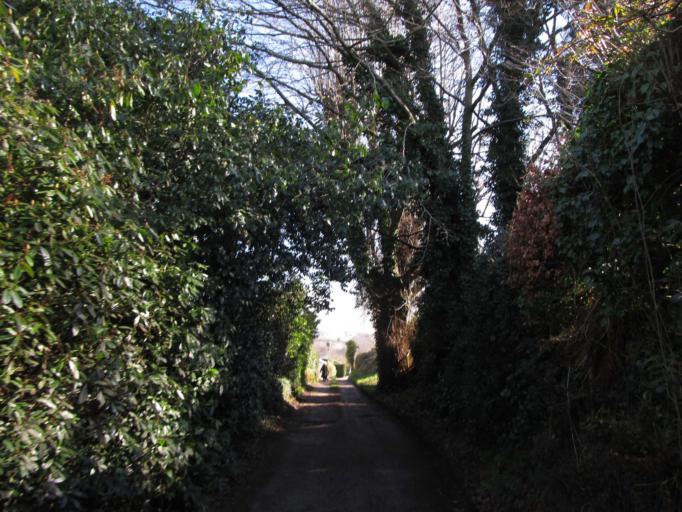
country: GB
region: England
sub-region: West Sussex
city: Petworth
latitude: 50.9850
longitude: -0.6039
